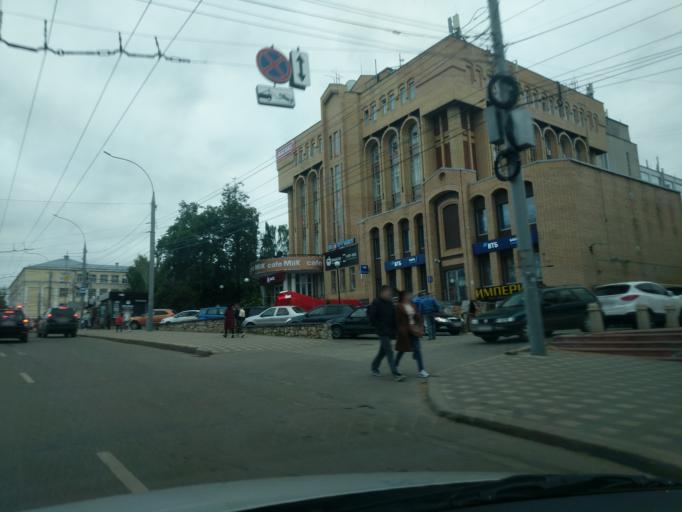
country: RU
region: Kirov
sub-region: Kirovo-Chepetskiy Rayon
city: Kirov
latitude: 58.5950
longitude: 49.6686
